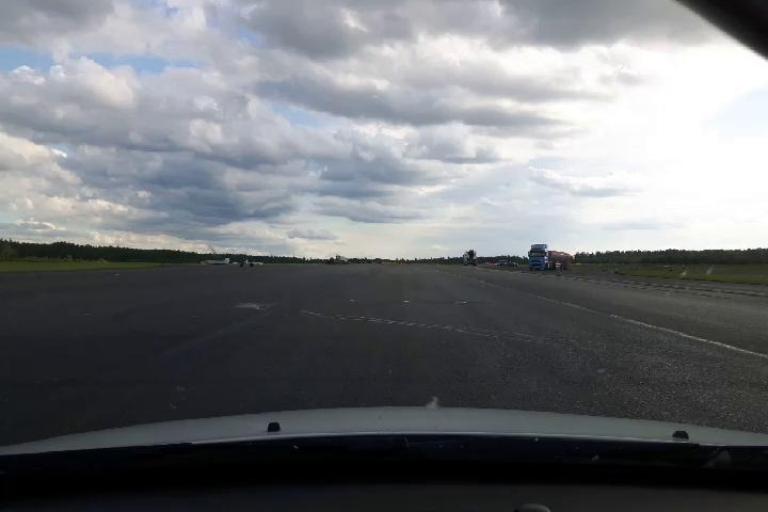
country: SE
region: Stockholm
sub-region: Sigtuna Kommun
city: Rosersberg
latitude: 59.6266
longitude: 17.9506
